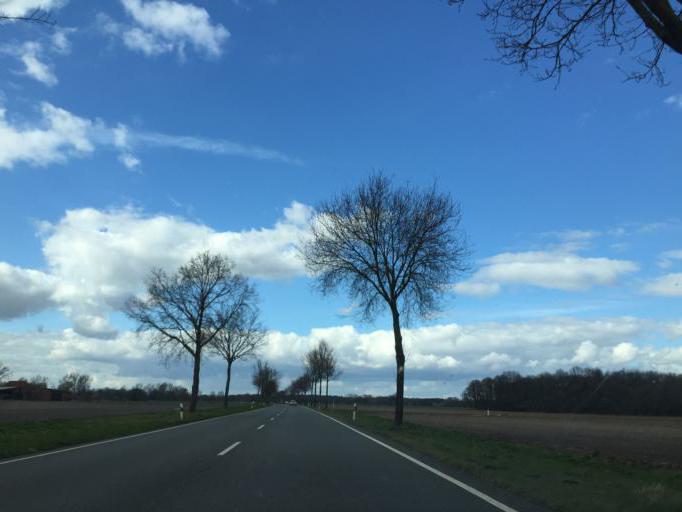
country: DE
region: Lower Saxony
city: Broeckel
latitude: 52.5263
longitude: 10.2200
